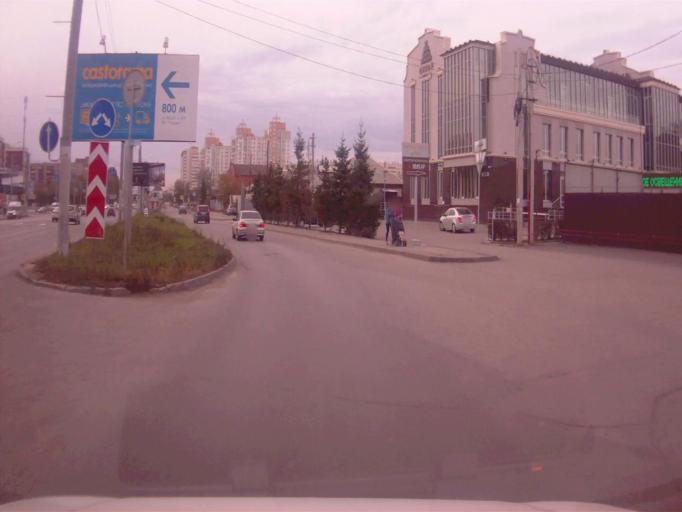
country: RU
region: Chelyabinsk
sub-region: Gorod Chelyabinsk
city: Chelyabinsk
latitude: 55.1788
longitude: 61.3603
